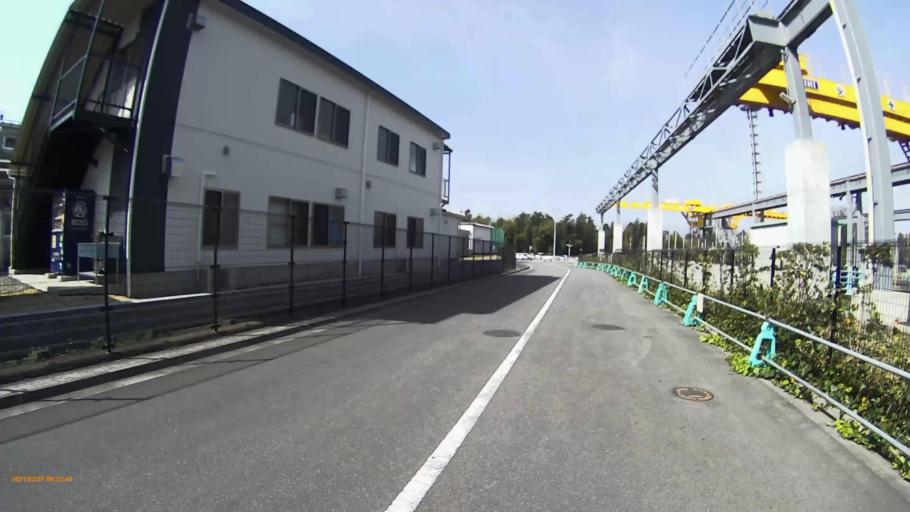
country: JP
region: Kanagawa
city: Minami-rinkan
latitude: 35.4444
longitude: 139.4157
